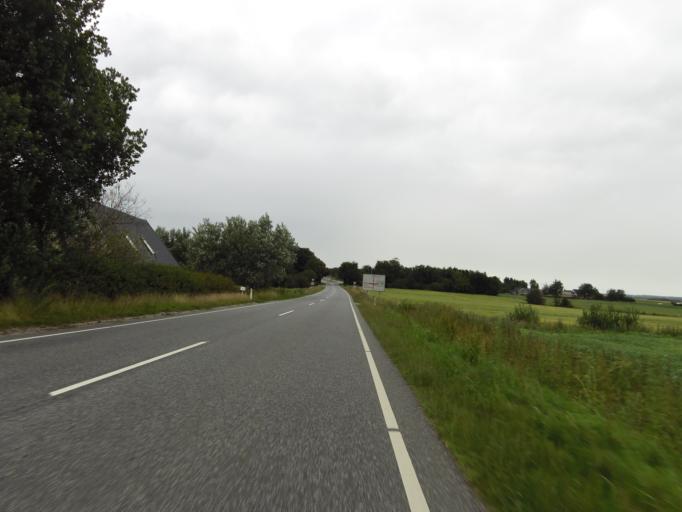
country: DK
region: South Denmark
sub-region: Tonder Kommune
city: Logumkloster
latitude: 55.1659
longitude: 8.9639
